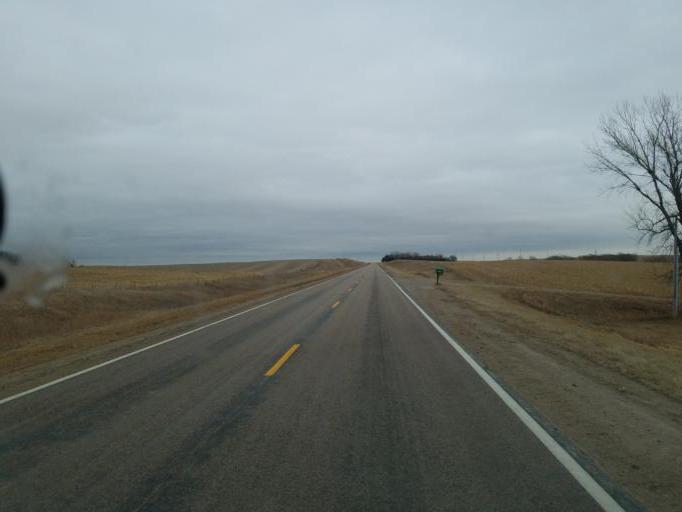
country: US
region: Nebraska
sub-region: Knox County
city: Bloomfield
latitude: 42.5977
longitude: -97.5808
